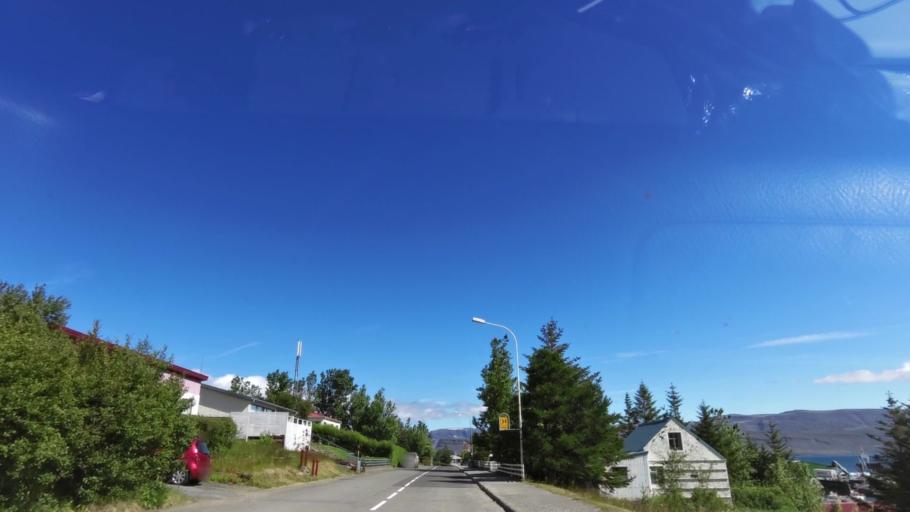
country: IS
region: Westfjords
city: Isafjoerdur
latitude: 65.6841
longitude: -23.6047
